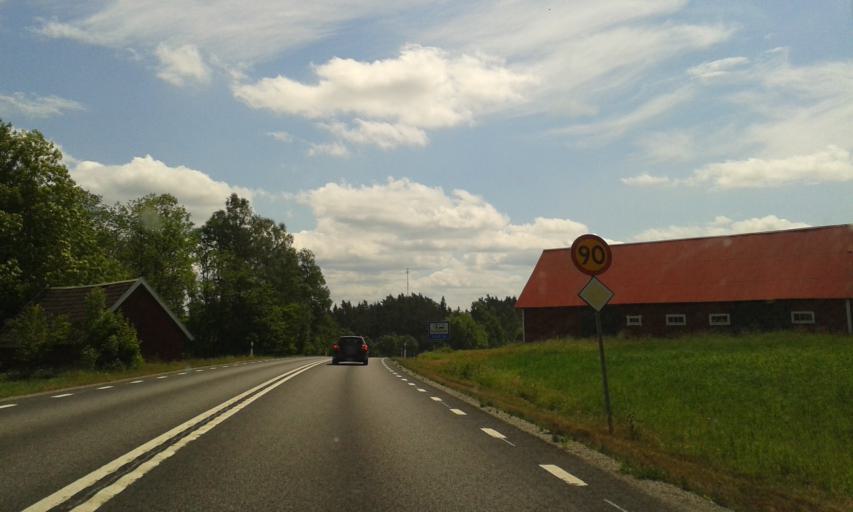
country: SE
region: Joenkoeping
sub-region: Varnamo Kommun
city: Rydaholm
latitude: 56.9963
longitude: 14.2882
